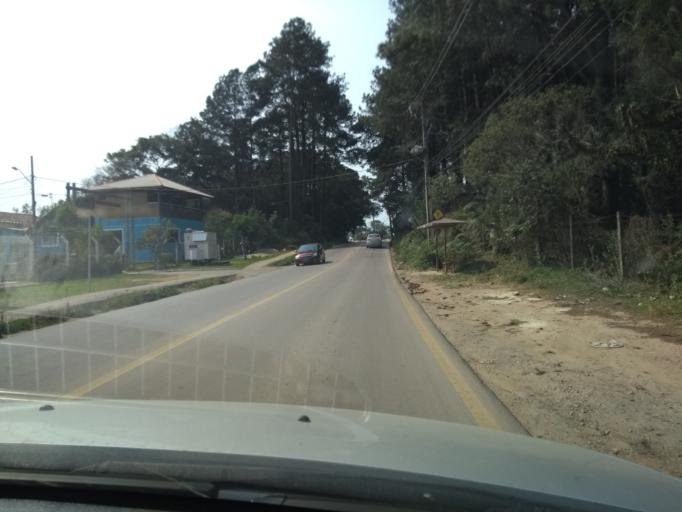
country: BR
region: Parana
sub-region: Araucaria
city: Araucaria
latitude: -25.6047
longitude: -49.3281
